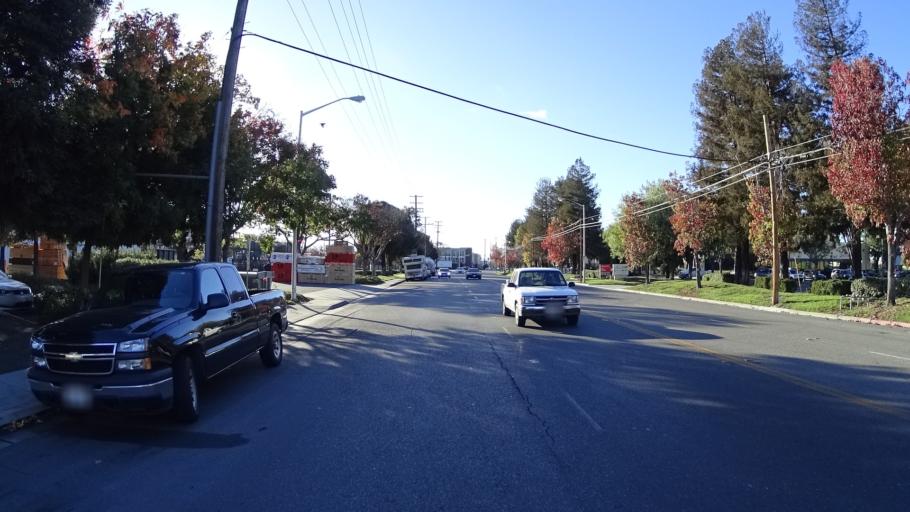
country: US
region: California
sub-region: Santa Clara County
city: Santa Clara
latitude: 37.3662
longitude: -121.9476
